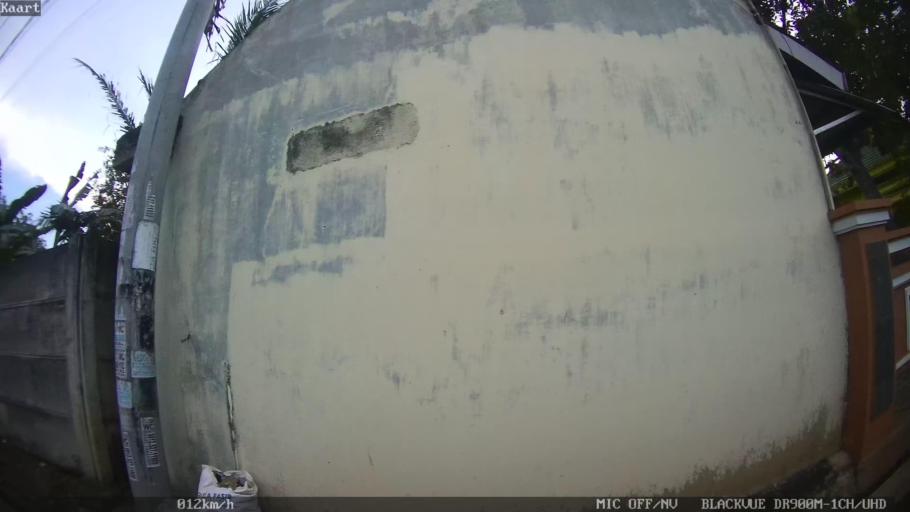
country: ID
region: Lampung
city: Kedaton
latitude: -5.3922
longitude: 105.2054
